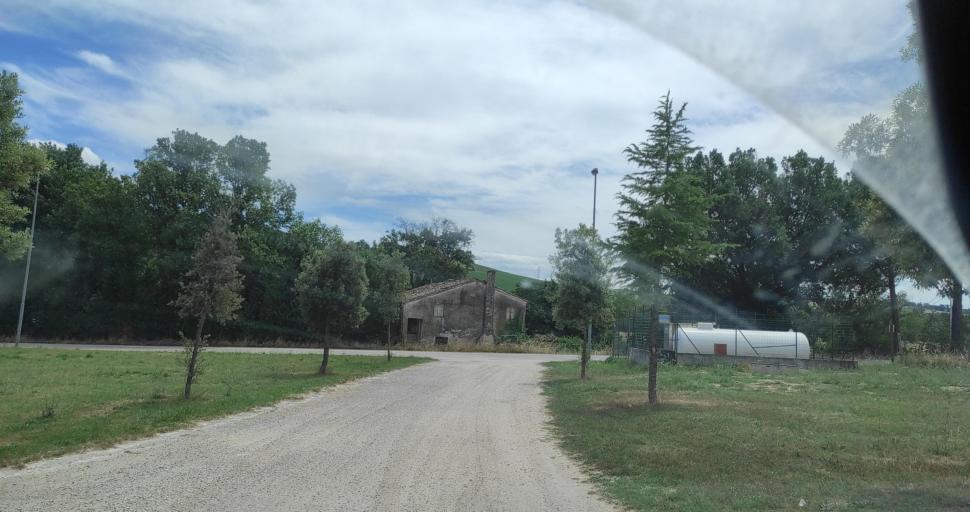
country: IT
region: The Marches
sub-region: Provincia di Macerata
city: Urbisaglia
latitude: 43.2073
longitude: 13.3922
